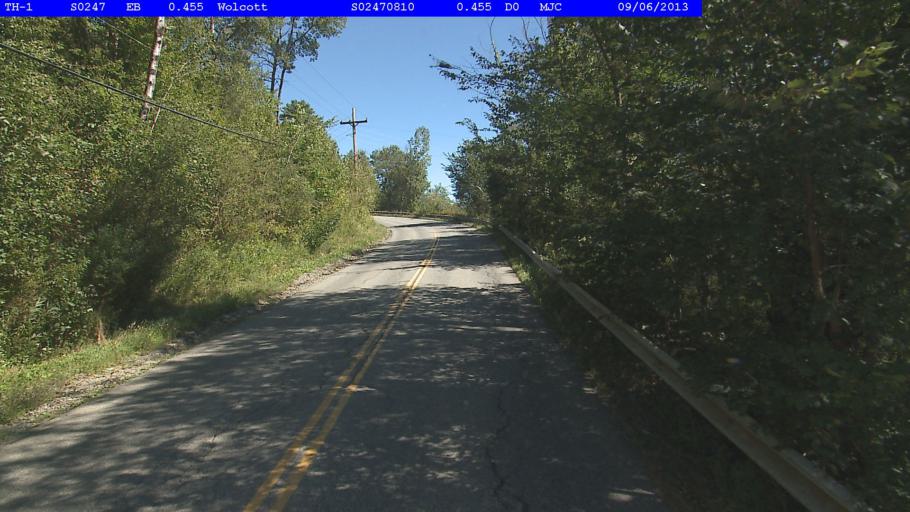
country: US
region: Vermont
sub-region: Lamoille County
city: Morrisville
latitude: 44.5647
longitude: -72.4863
